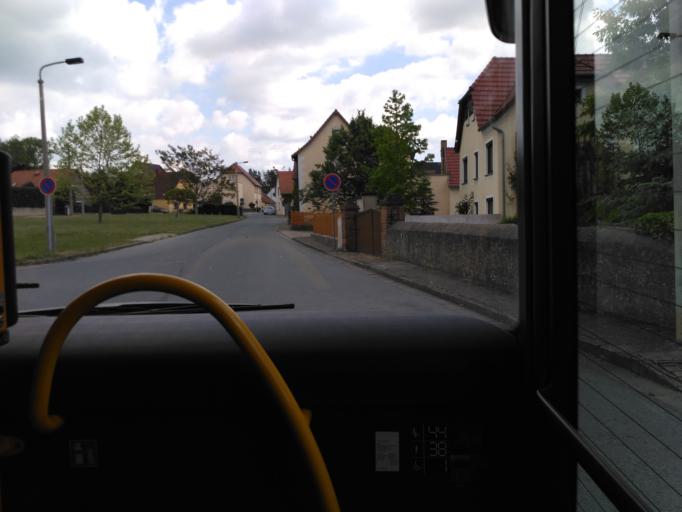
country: DE
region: Saxony
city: Glaubitz
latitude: 51.3241
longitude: 13.3792
